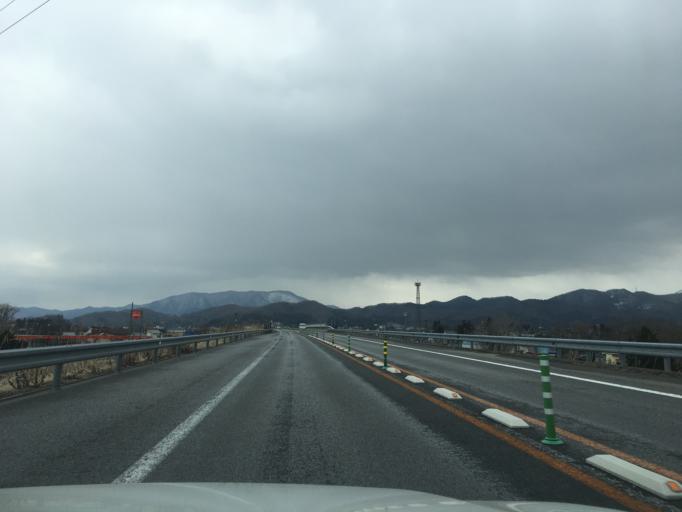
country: JP
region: Aomori
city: Aomori Shi
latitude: 40.7980
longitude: 140.7817
